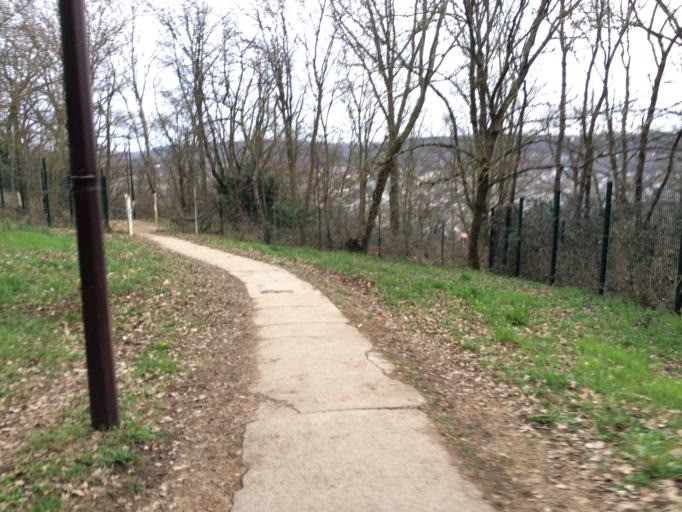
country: FR
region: Ile-de-France
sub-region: Departement de l'Essonne
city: Vauhallan
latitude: 48.7087
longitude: 2.2113
